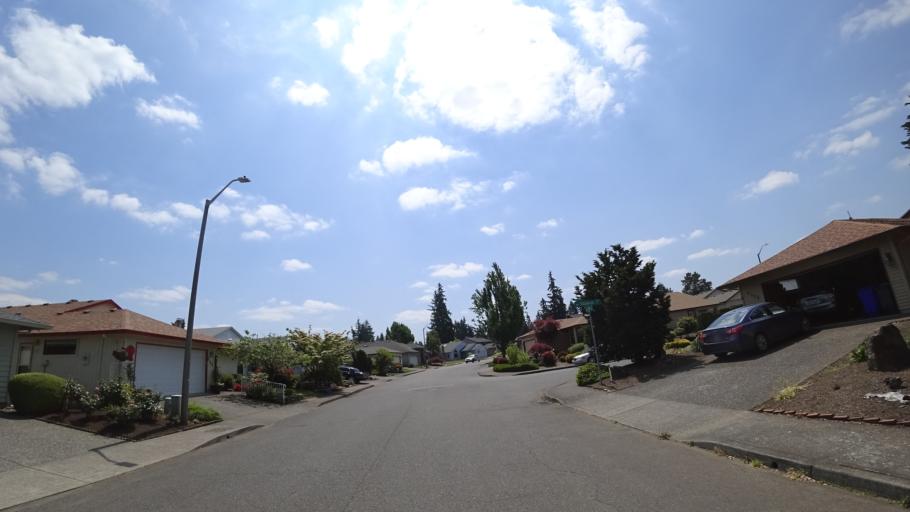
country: US
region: Oregon
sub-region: Multnomah County
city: Fairview
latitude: 45.5387
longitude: -122.5007
